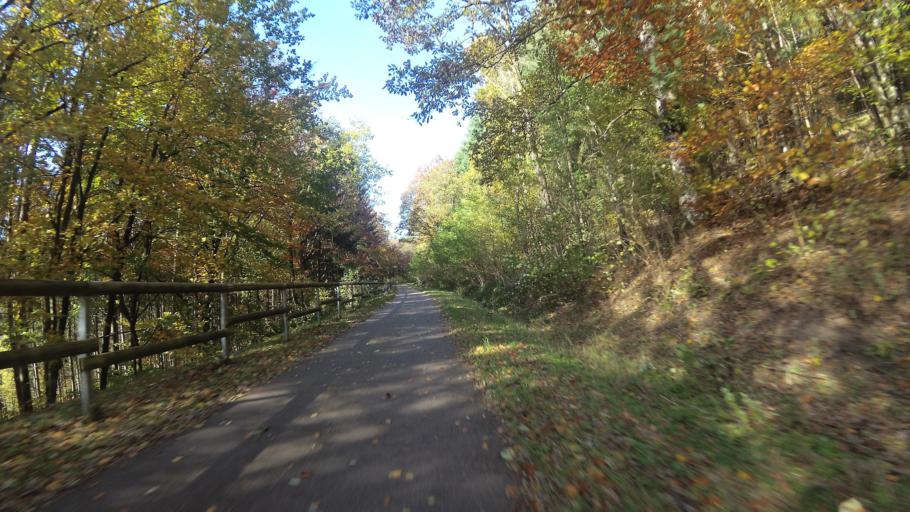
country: DE
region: Rheinland-Pfalz
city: Hentern
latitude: 49.6115
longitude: 6.6990
